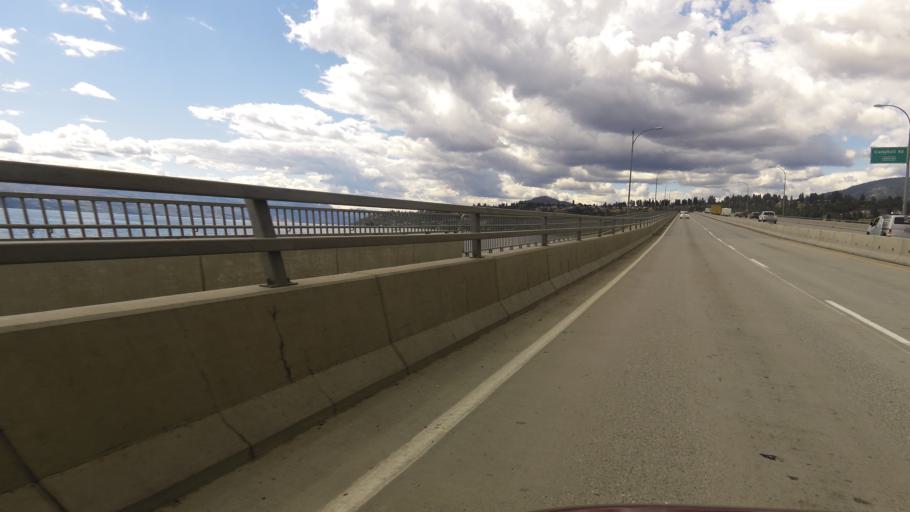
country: CA
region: British Columbia
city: Kelowna
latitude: 49.8794
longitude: -119.5111
